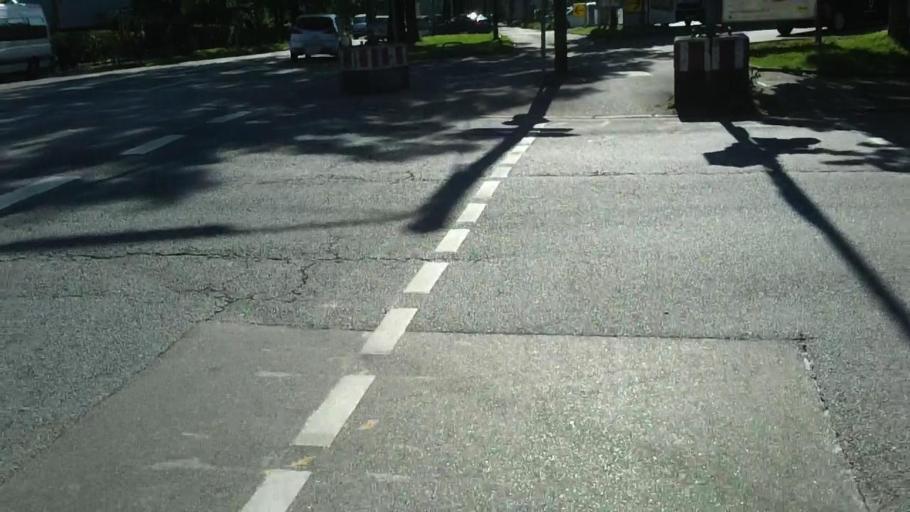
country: DE
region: Bavaria
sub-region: Upper Bavaria
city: Karlsfeld
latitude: 48.1847
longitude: 11.5052
